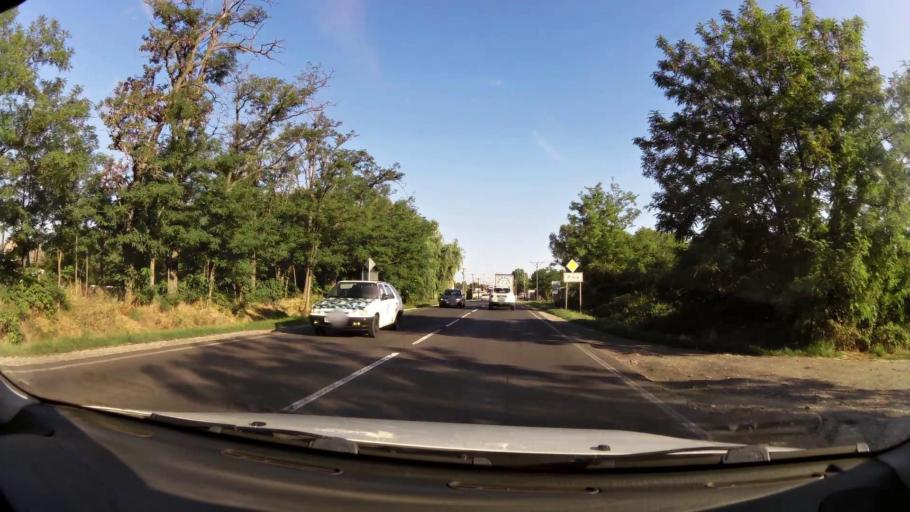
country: HU
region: Pest
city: Pilis
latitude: 47.2806
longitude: 19.5535
